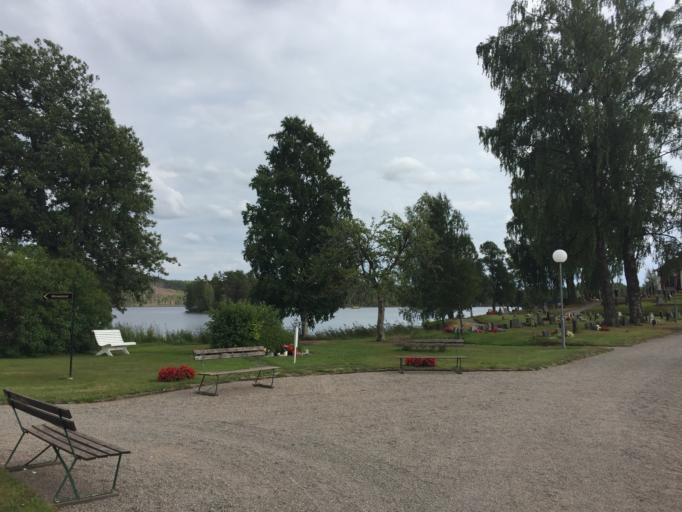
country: SE
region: Vaermland
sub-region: Filipstads Kommun
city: Lesjofors
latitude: 60.0321
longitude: 14.1283
